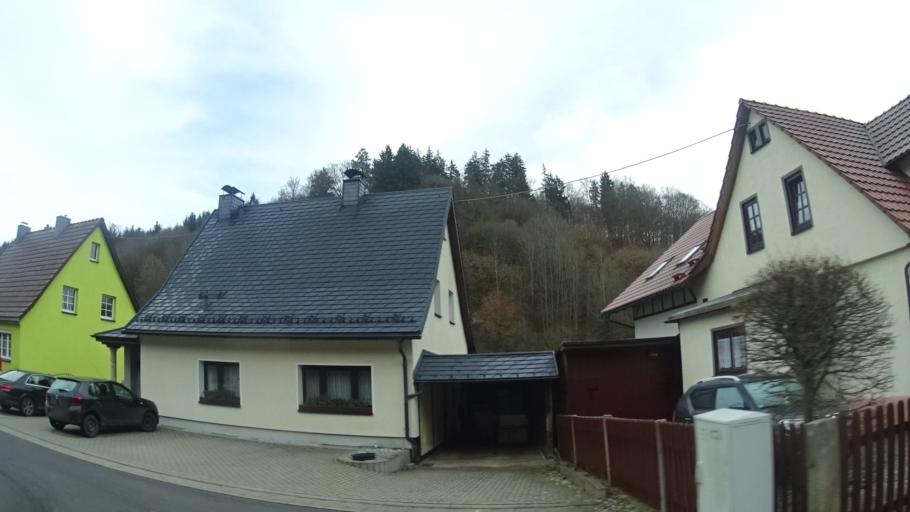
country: DE
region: Thuringia
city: Pappenheim
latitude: 50.8014
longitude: 10.4702
